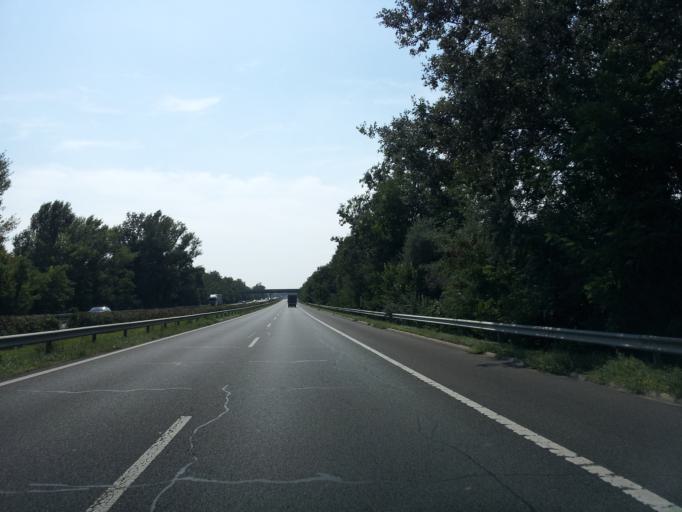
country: HU
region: Fejer
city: Martonvasar
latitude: 47.3235
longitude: 18.7657
